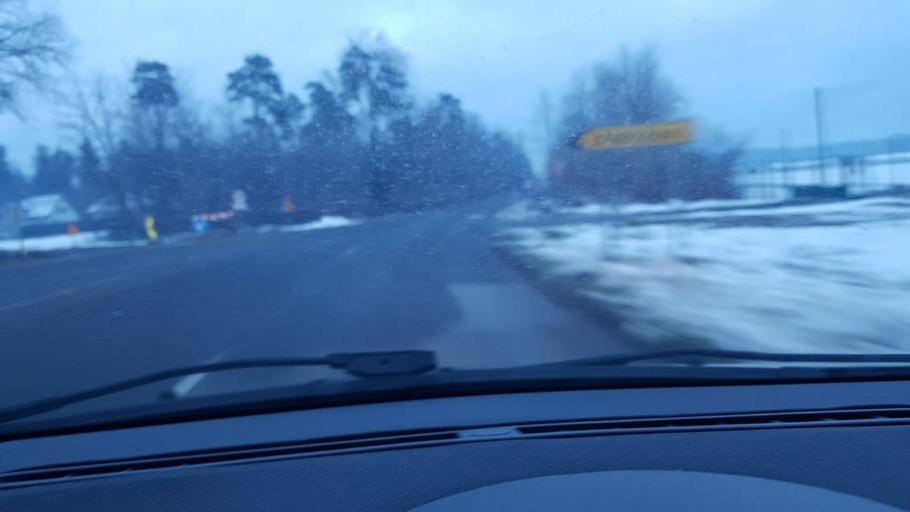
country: SI
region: Kidricevo
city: Kidricevo
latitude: 46.3935
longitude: 15.8102
